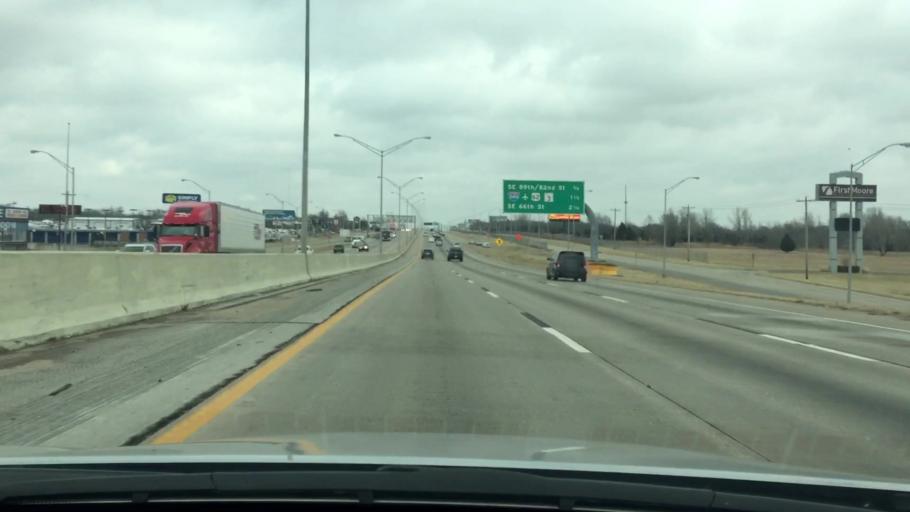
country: US
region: Oklahoma
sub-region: Cleveland County
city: Moore
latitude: 35.3641
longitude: -97.4948
